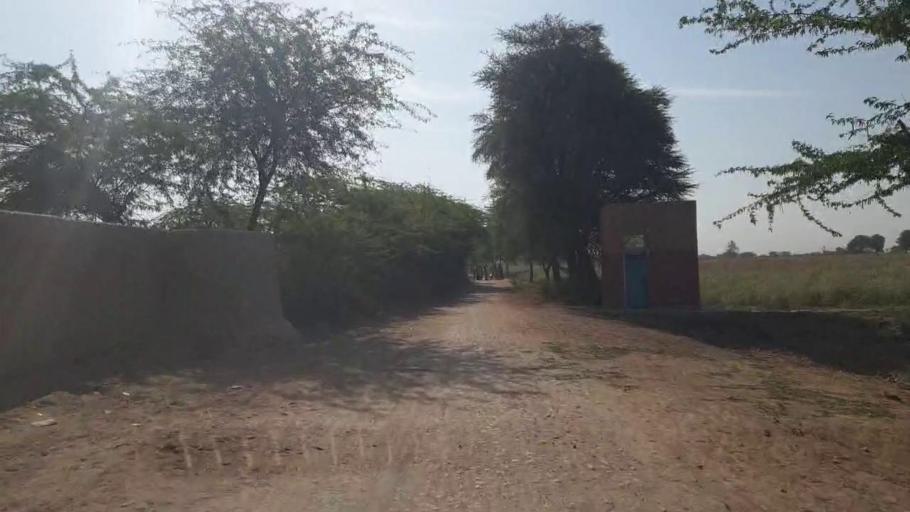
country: PK
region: Sindh
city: Umarkot
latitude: 25.2992
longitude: 69.6774
